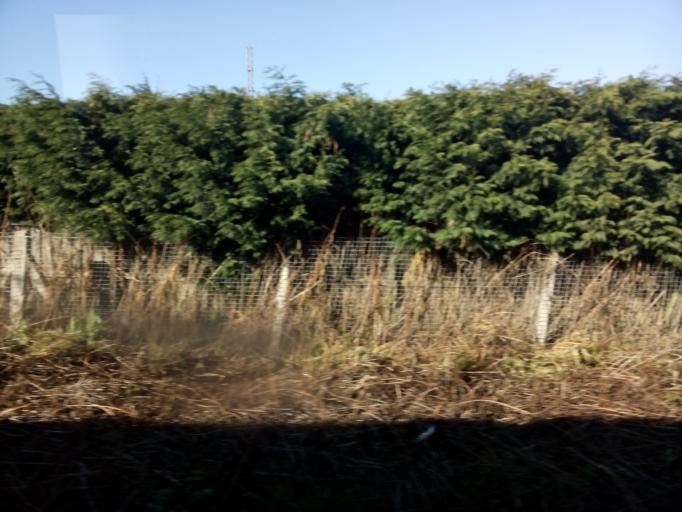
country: GB
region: England
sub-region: Northumberland
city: Morpeth
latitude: 55.1561
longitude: -1.6838
